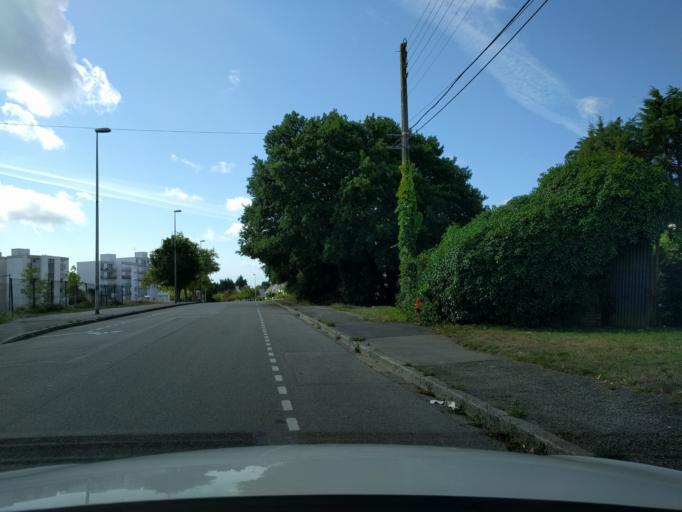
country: FR
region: Brittany
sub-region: Departement du Morbihan
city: Lorient
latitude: 47.7487
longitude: -3.3936
